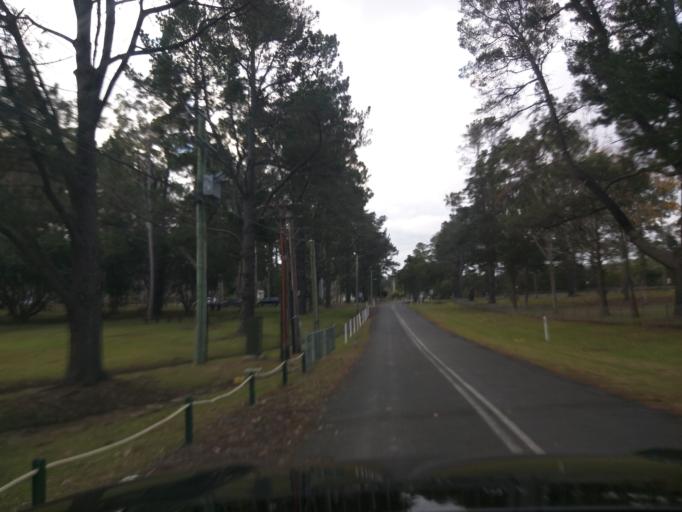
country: AU
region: New South Wales
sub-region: Wollongong
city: Mount Keira
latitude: -34.3271
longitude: 150.7458
